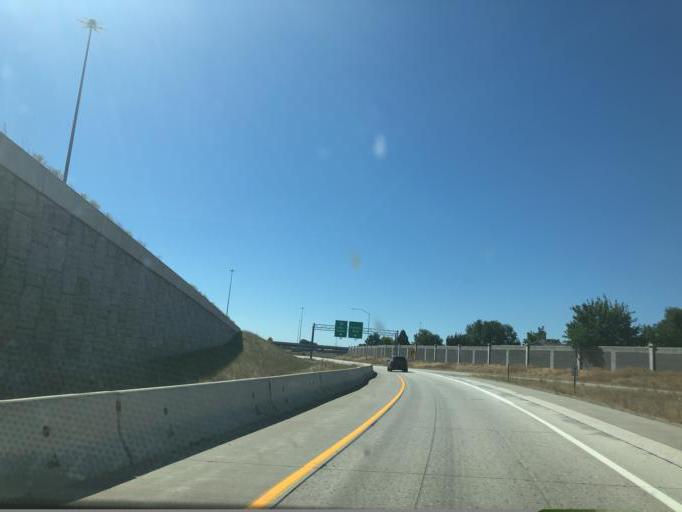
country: US
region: Idaho
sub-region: Ada County
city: Garden City
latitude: 43.5943
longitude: -116.2814
